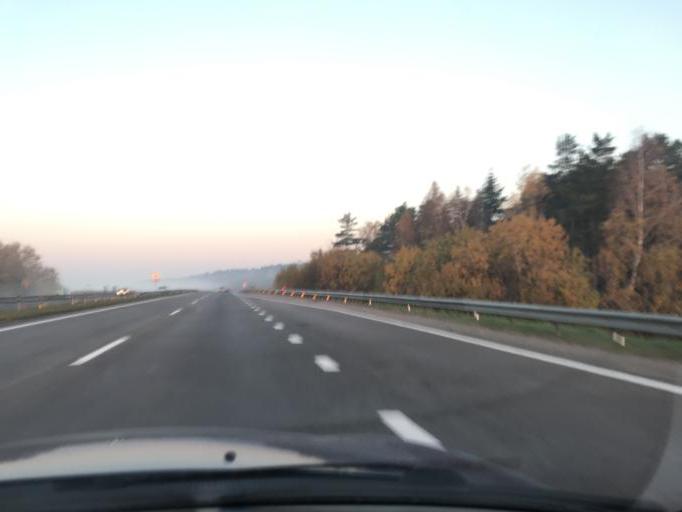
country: BY
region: Minsk
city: Khatsyezhyna
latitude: 53.9172
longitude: 27.3243
